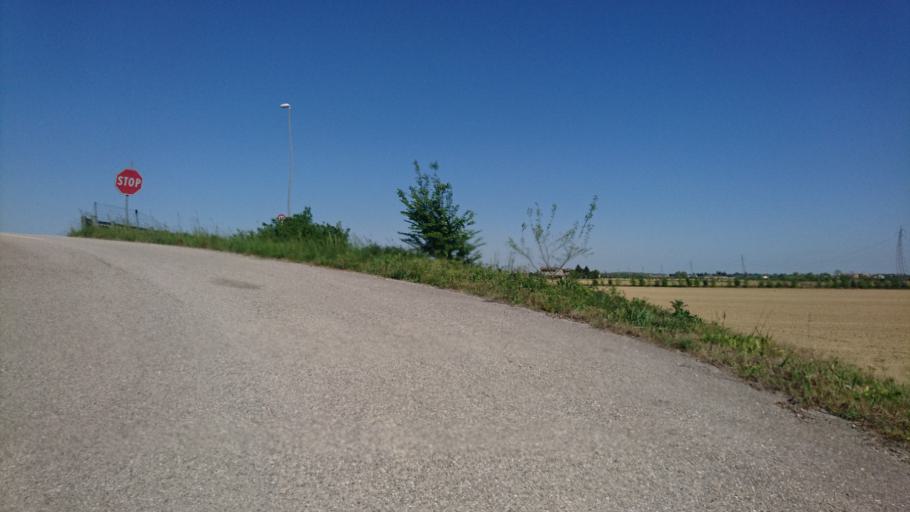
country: IT
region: Veneto
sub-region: Provincia di Venezia
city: Marcon-Gaggio-Colmello
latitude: 45.5734
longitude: 12.2821
